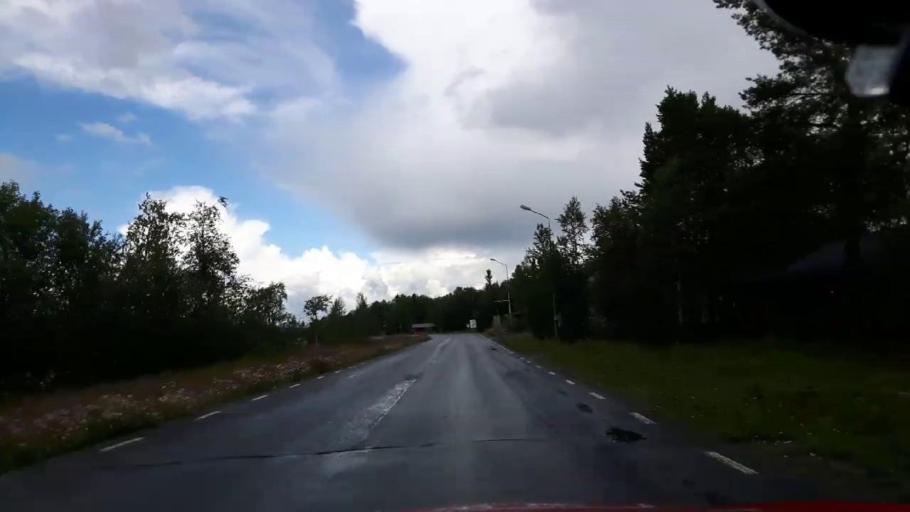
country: SE
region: Vaesterbotten
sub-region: Vilhelmina Kommun
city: Sjoberg
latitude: 64.9698
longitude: 15.3703
